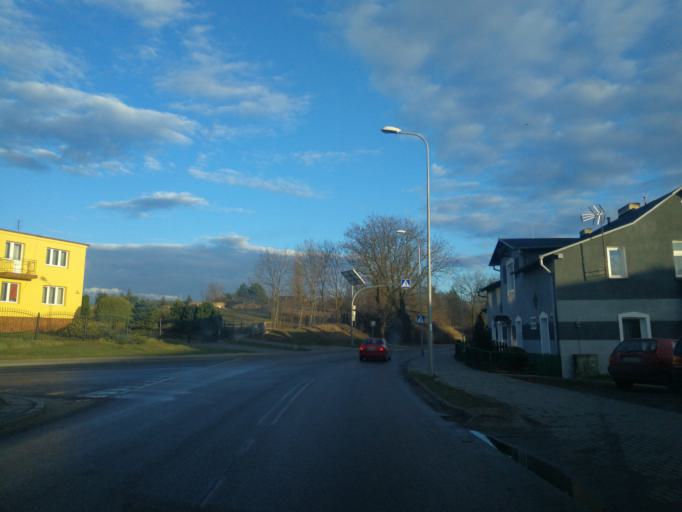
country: PL
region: Kujawsko-Pomorskie
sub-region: Powiat torunski
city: Chelmza
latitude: 53.1931
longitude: 18.6122
